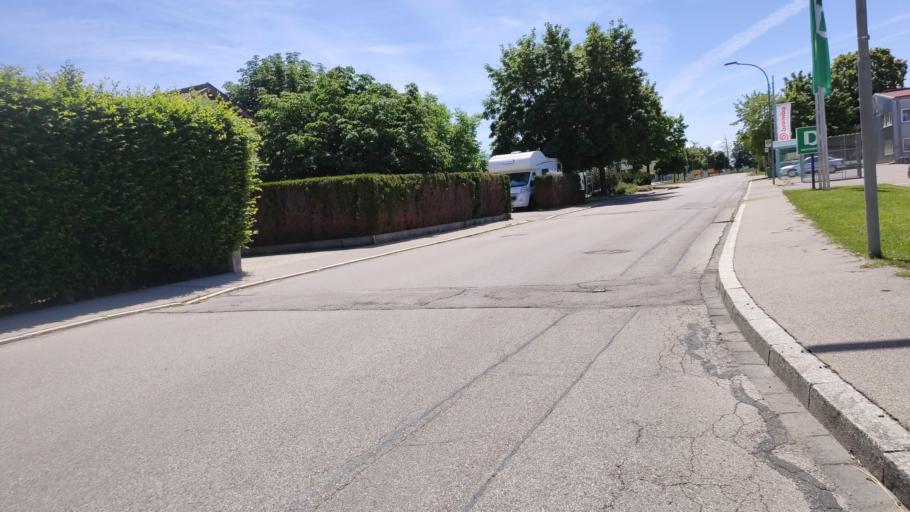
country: DE
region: Bavaria
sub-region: Swabia
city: Bad Worishofen
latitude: 48.0207
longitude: 10.6025
